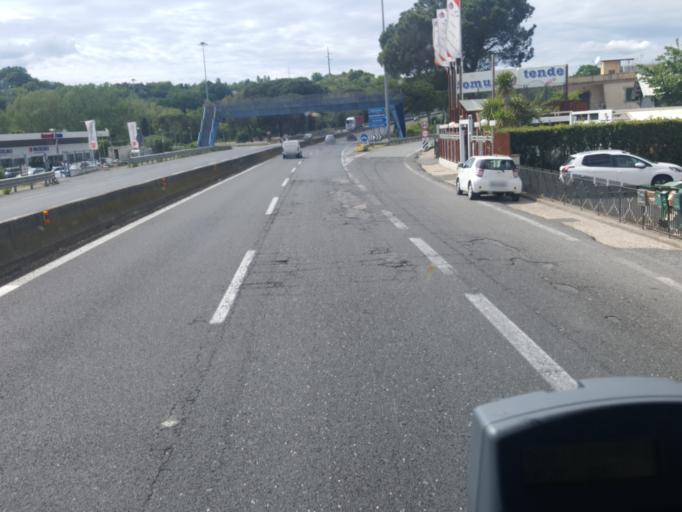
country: IT
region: Latium
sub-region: Citta metropolitana di Roma Capitale
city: Ara Nova
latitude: 41.9067
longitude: 12.2655
